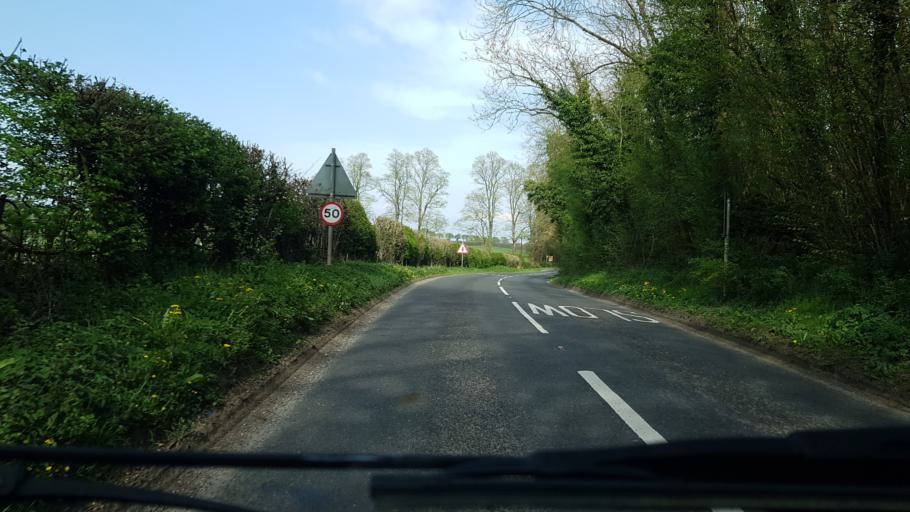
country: GB
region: England
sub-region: Hampshire
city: Overton
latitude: 51.2466
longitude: -1.2150
